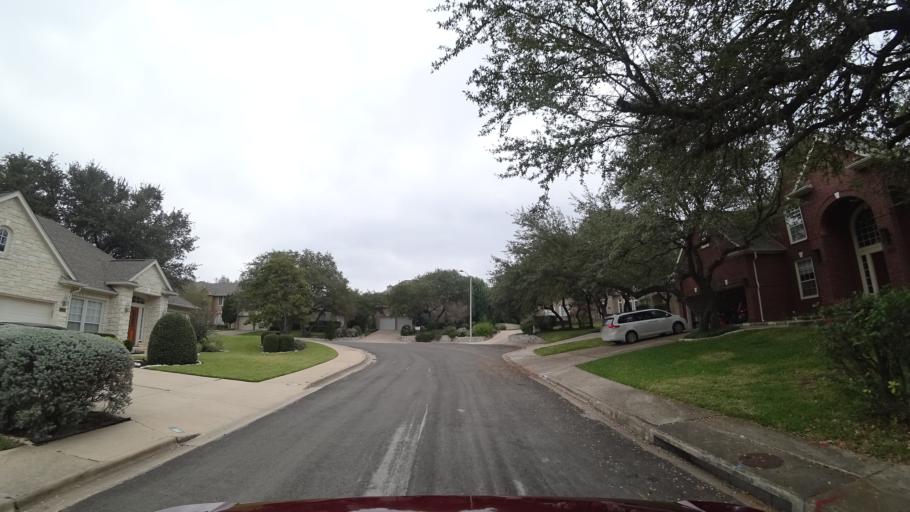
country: US
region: Texas
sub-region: Williamson County
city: Anderson Mill
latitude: 30.4348
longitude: -97.8286
